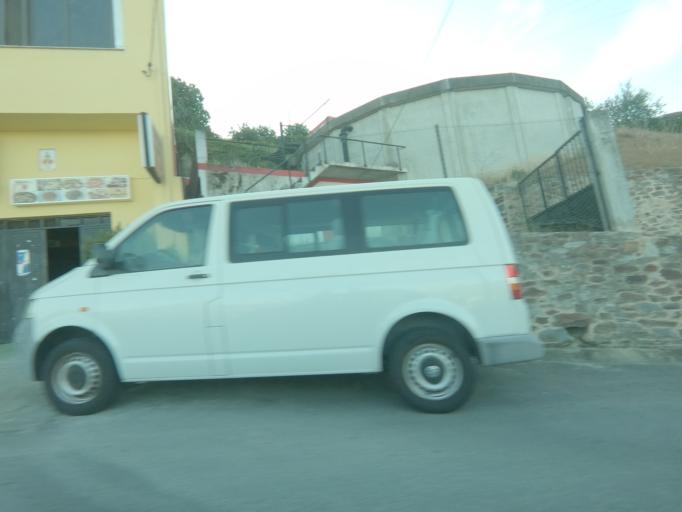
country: PT
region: Vila Real
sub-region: Peso da Regua
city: Godim
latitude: 41.1655
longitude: -7.8098
